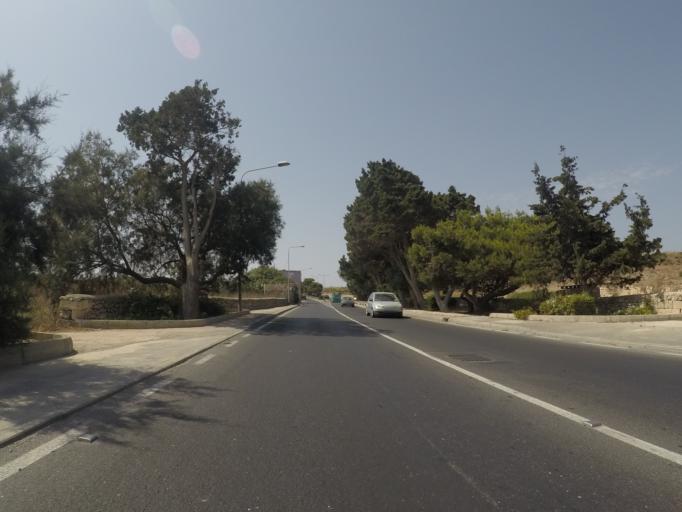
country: MT
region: L-Imdina
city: Imdina
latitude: 35.8936
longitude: 14.4095
